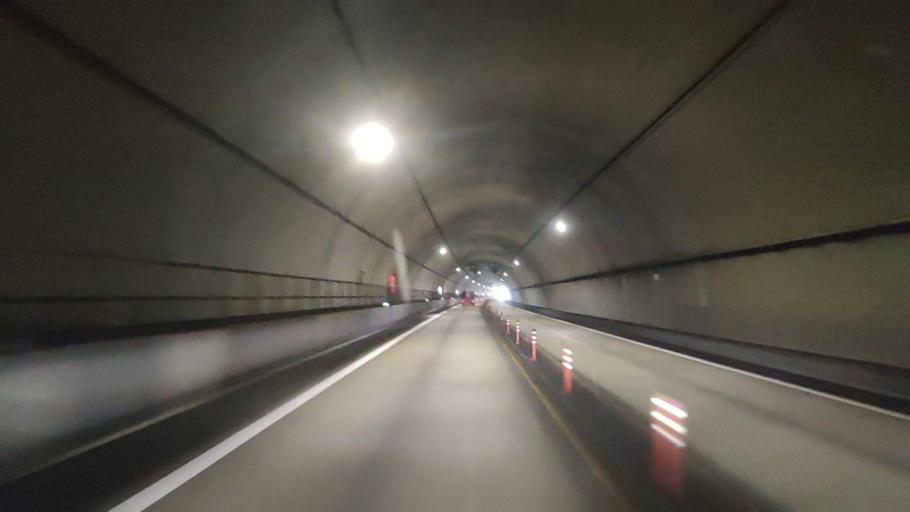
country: JP
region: Wakayama
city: Tanabe
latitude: 33.5505
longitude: 135.5150
